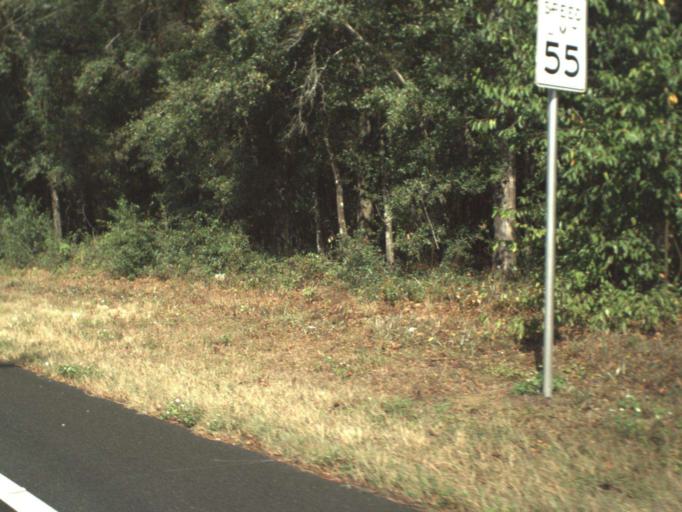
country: US
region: Florida
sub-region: Gadsden County
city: Midway
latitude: 30.4416
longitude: -84.3895
